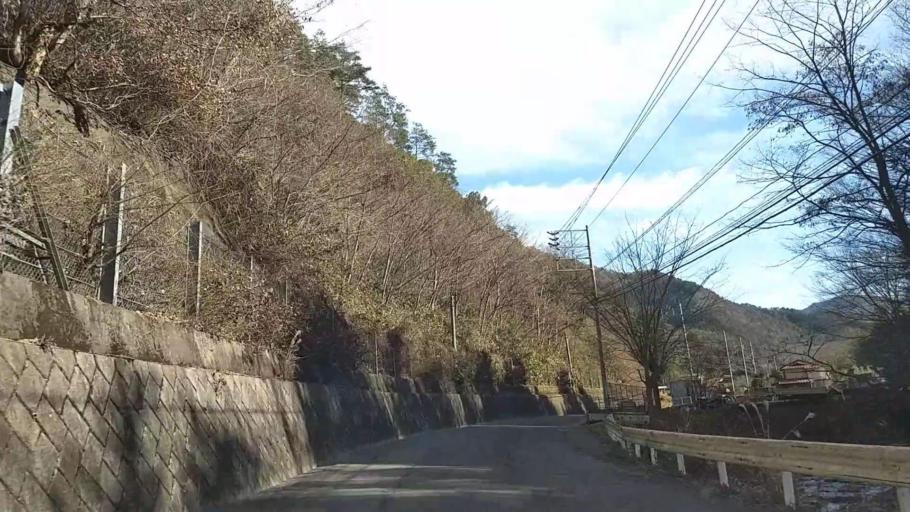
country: JP
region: Yamanashi
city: Otsuki
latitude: 35.5322
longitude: 138.9140
